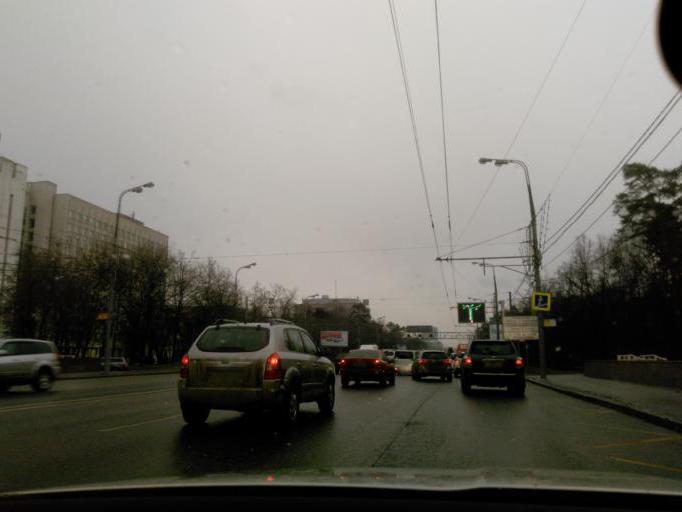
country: RU
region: Moscow
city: Pokrovskoye-Streshnevo
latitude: 55.8126
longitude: 37.4764
